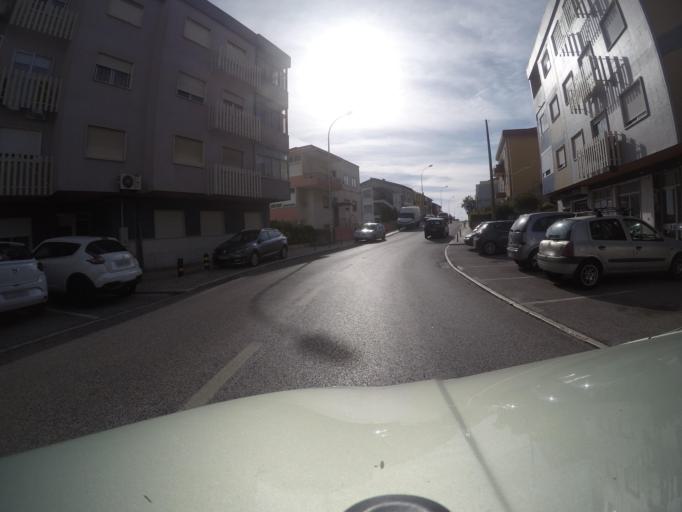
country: PT
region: Lisbon
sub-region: Amadora
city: Amadora
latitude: 38.7642
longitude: -9.2318
